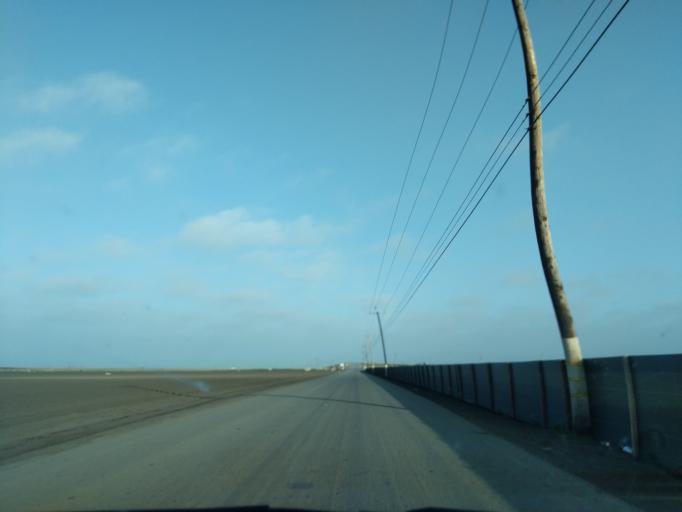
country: US
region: California
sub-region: Monterey County
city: Castroville
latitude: 36.7506
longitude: -121.7766
